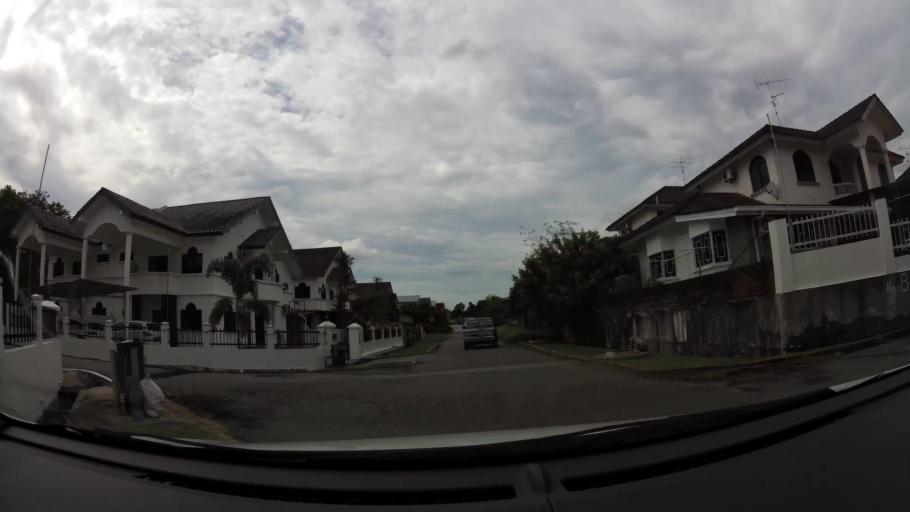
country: BN
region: Brunei and Muara
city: Bandar Seri Begawan
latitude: 4.8847
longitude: 114.8987
